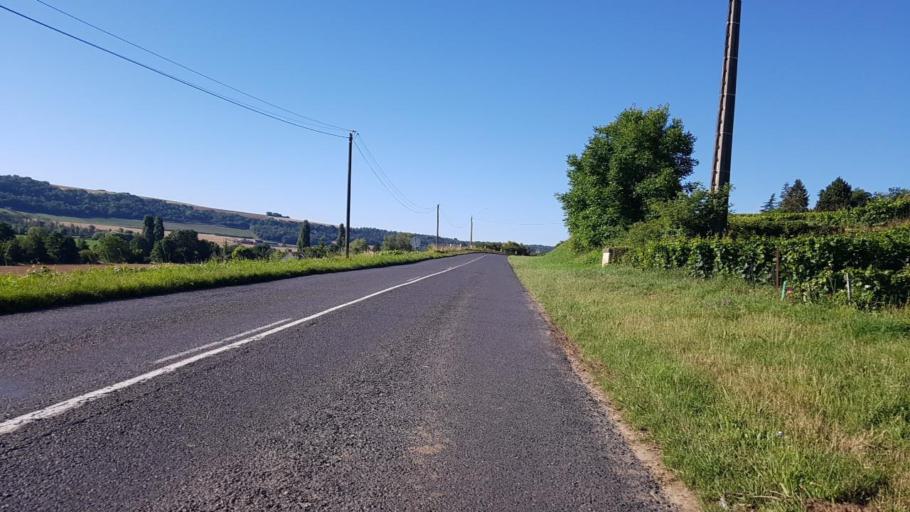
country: FR
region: Picardie
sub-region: Departement de l'Aisne
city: Essomes-sur-Marne
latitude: 49.0119
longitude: 3.3755
